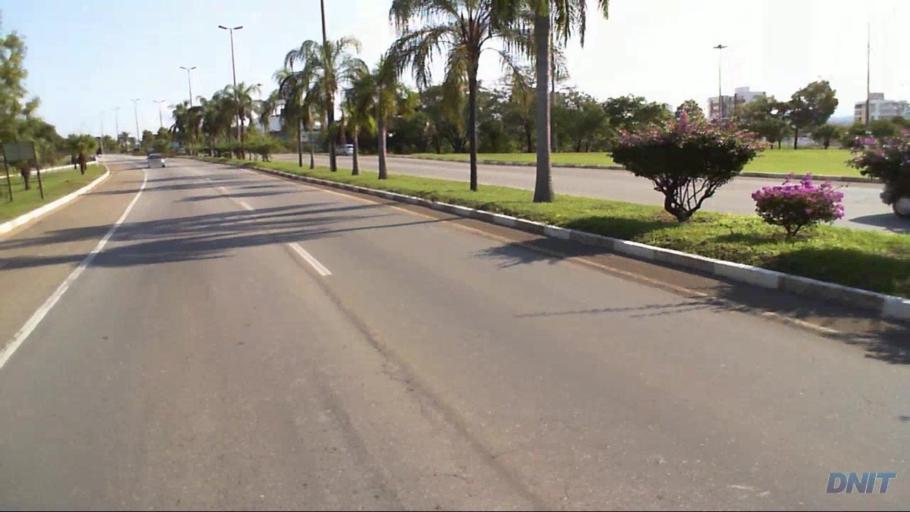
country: BR
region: Minas Gerais
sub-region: Ipatinga
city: Ipatinga
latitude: -19.4724
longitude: -42.5406
